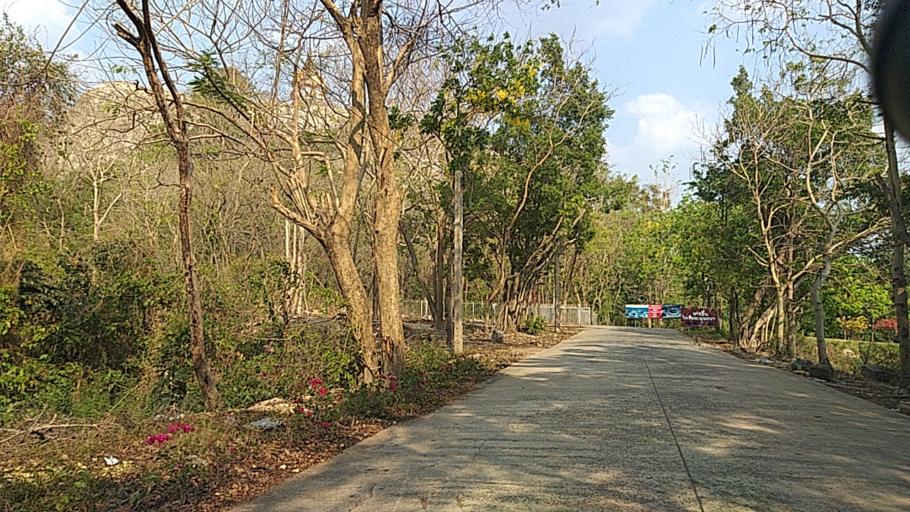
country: TH
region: Sara Buri
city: Saraburi
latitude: 14.4607
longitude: 100.9468
